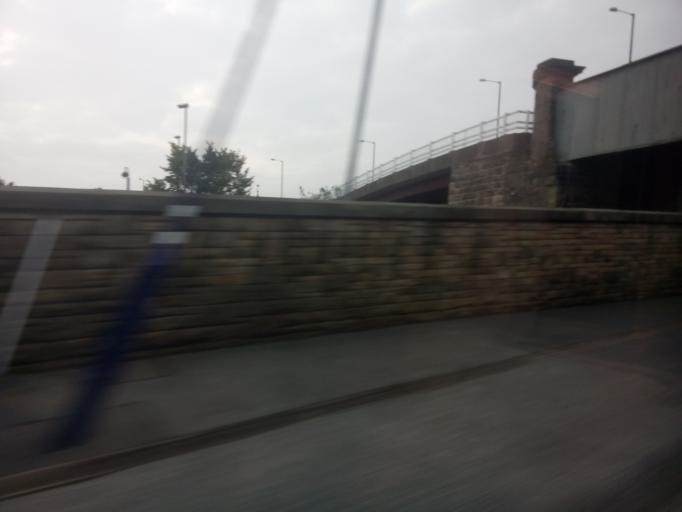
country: GB
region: England
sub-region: Kirklees
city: Dewsbury
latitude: 53.6914
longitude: -1.6336
